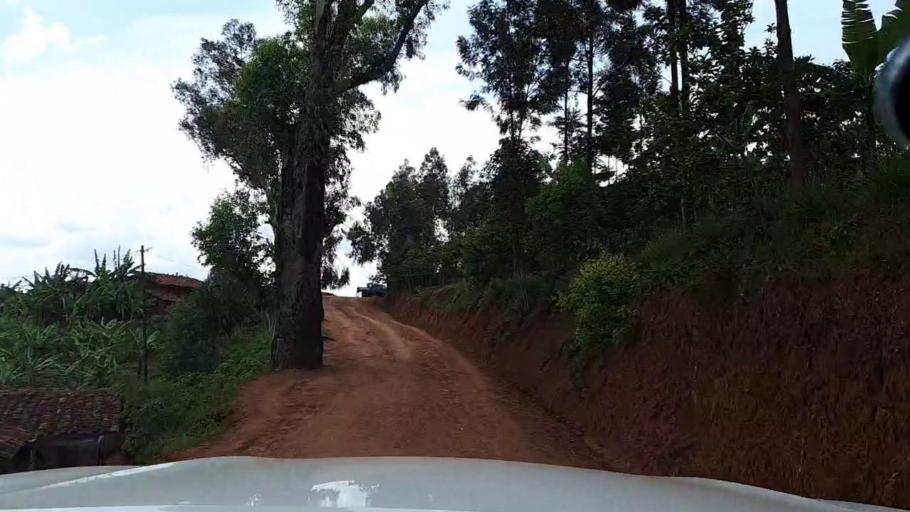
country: RW
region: Southern Province
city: Butare
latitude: -2.7543
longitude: 29.7534
